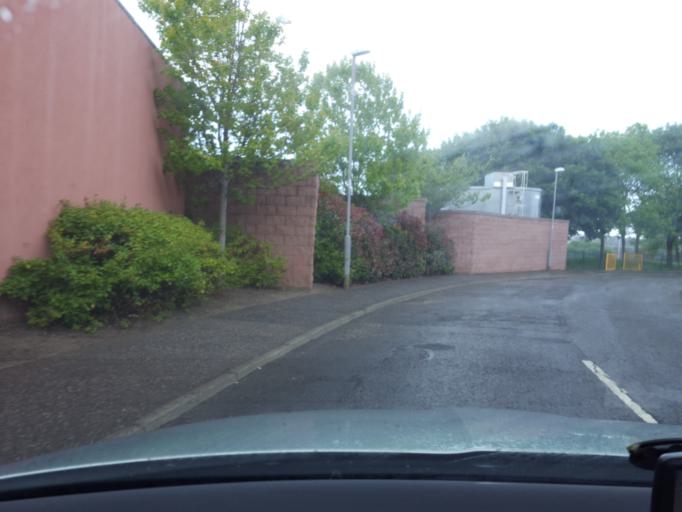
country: GB
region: Scotland
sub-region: Angus
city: Arbroath
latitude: 56.5619
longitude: -2.5923
